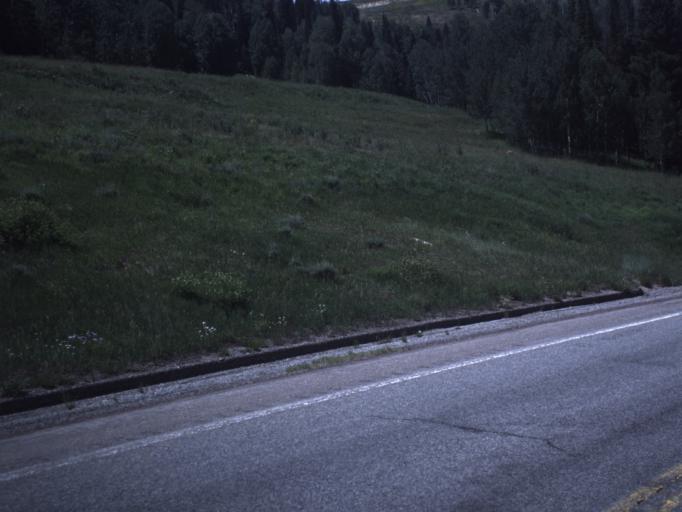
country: US
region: Utah
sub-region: Sanpete County
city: Fairview
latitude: 39.5856
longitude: -111.2427
